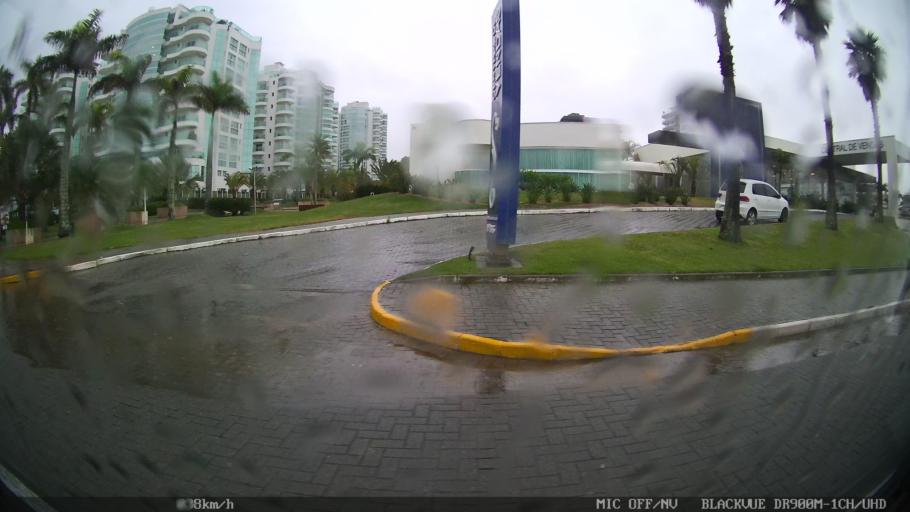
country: BR
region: Santa Catarina
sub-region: Balneario Camboriu
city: Balneario Camboriu
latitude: -26.9517
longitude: -48.6297
